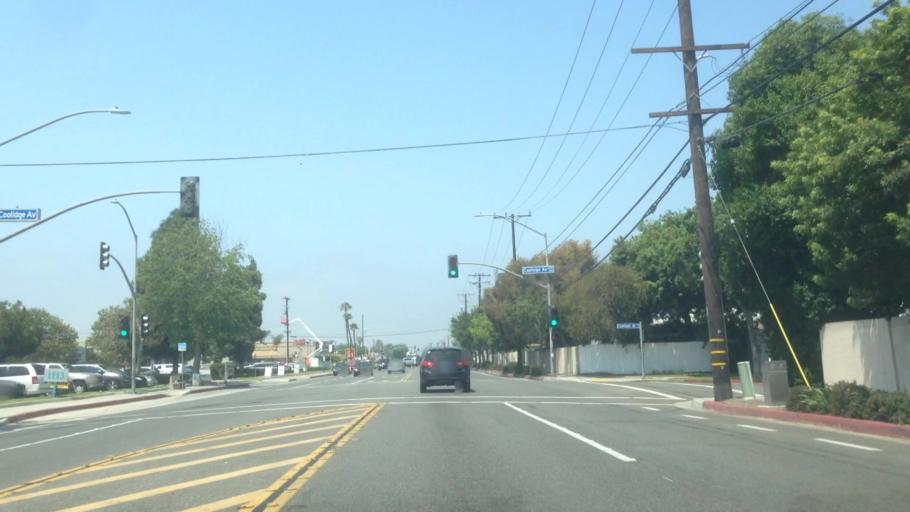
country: US
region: California
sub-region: Orange County
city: Costa Mesa
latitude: 33.6801
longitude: -117.9036
